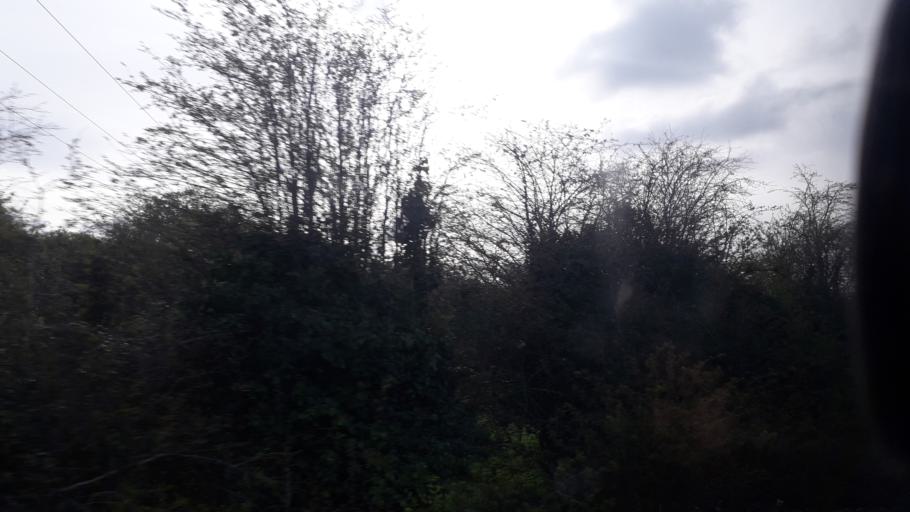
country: IE
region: Leinster
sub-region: Kildare
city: Kilcock
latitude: 53.4194
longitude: -6.7101
